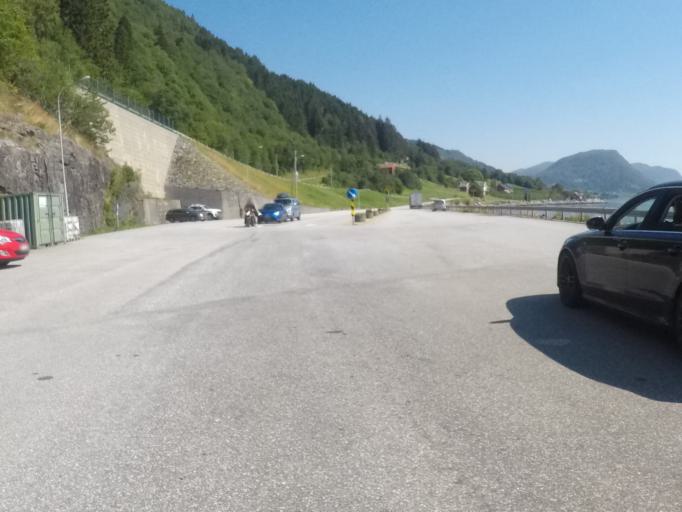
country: NO
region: More og Romsdal
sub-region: Vanylven
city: Fiska
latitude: 61.9140
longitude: 5.7244
